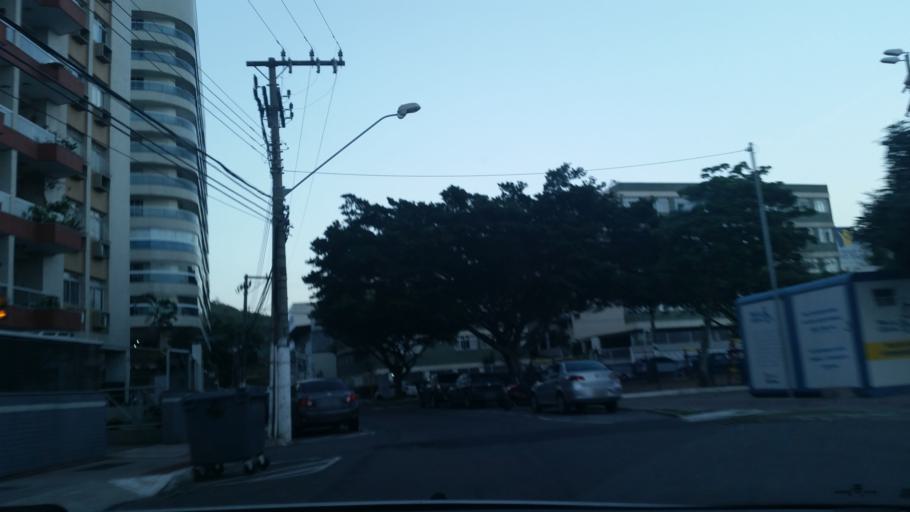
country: BR
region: Espirito Santo
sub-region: Vila Velha
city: Vila Velha
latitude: -20.3295
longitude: -40.2736
